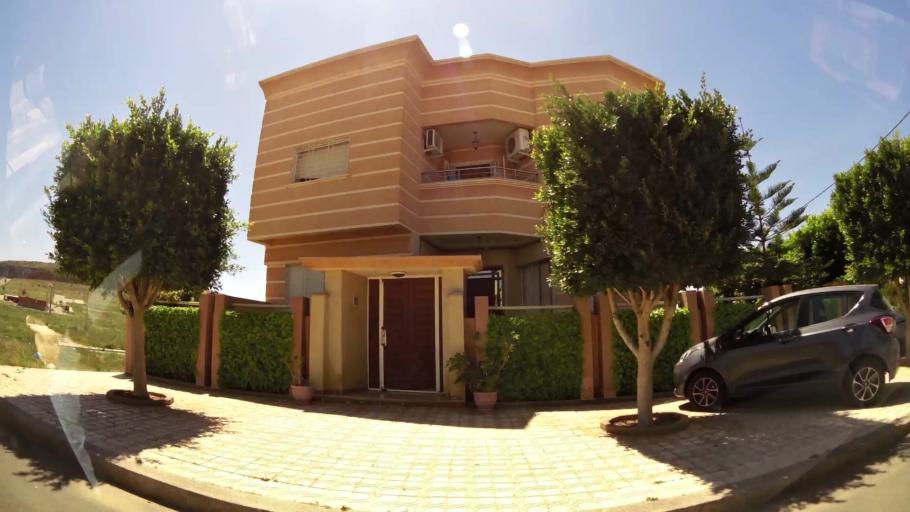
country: MA
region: Oriental
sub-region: Oujda-Angad
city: Oujda
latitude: 34.6516
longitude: -1.9154
